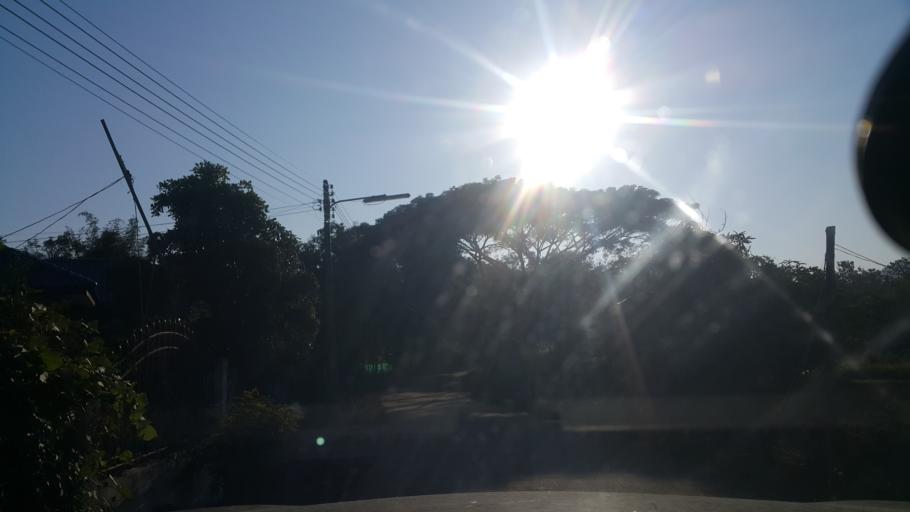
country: TH
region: Chiang Mai
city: Mae On
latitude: 18.7665
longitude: 99.2664
